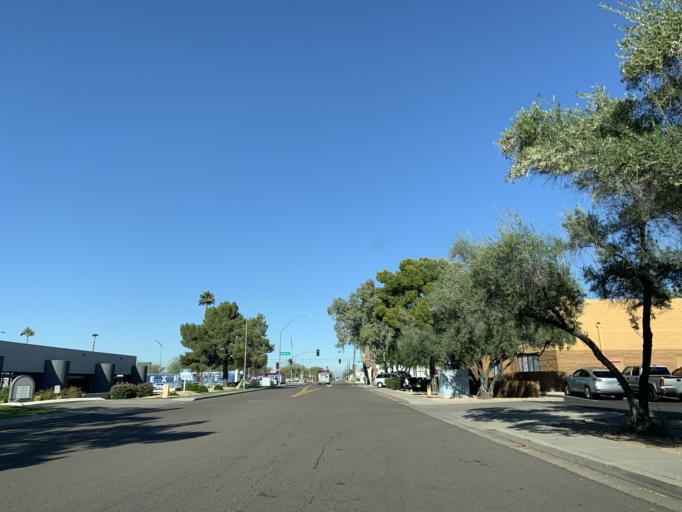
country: US
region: Arizona
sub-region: Maricopa County
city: Tempe
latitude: 33.4136
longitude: -111.8700
